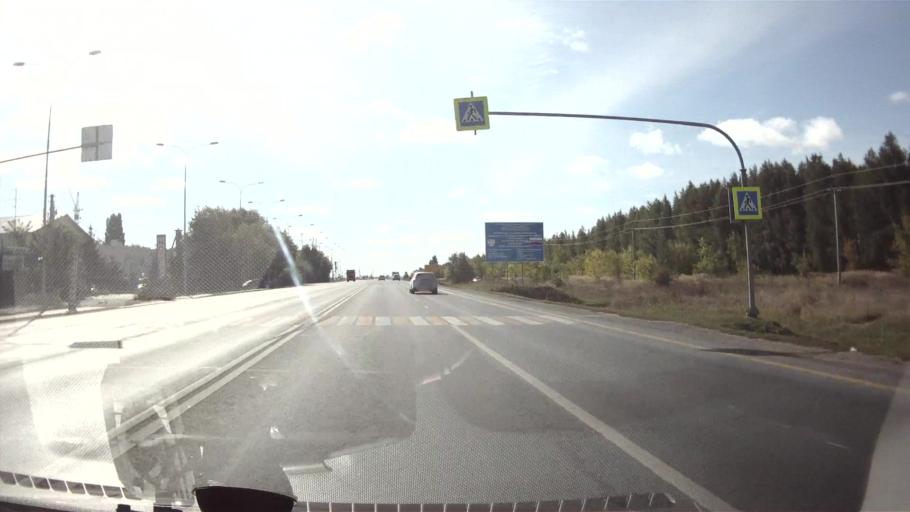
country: RU
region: Ulyanovsk
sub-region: Ulyanovskiy Rayon
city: Ulyanovsk
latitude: 54.2888
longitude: 48.2555
